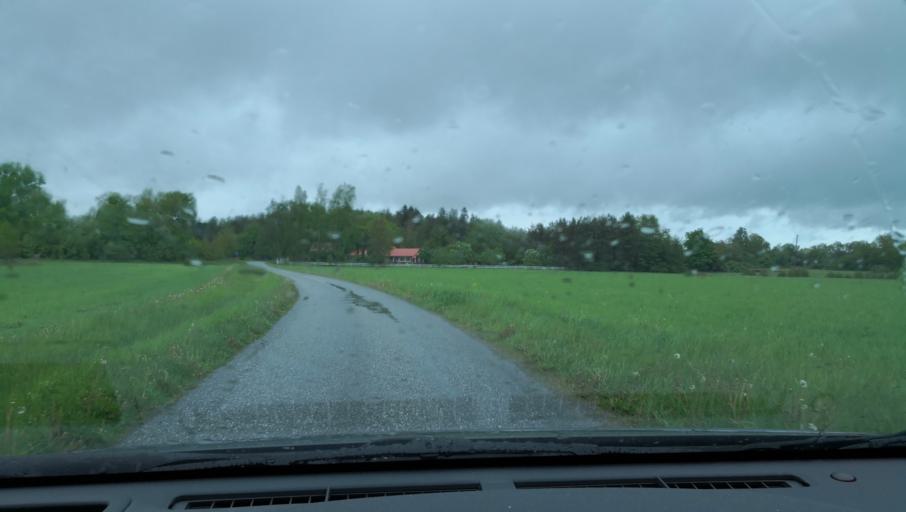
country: SE
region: Uppsala
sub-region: Enkopings Kommun
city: Orsundsbro
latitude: 59.7682
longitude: 17.3418
